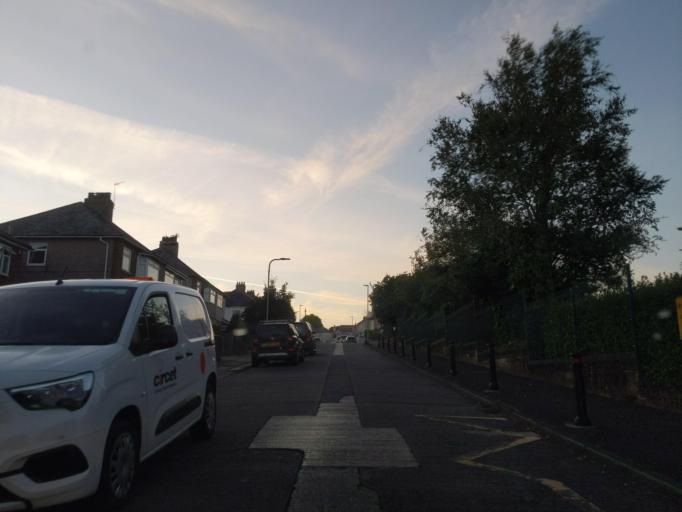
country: GB
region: England
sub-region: Plymouth
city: Plymouth
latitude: 50.3925
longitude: -4.1550
